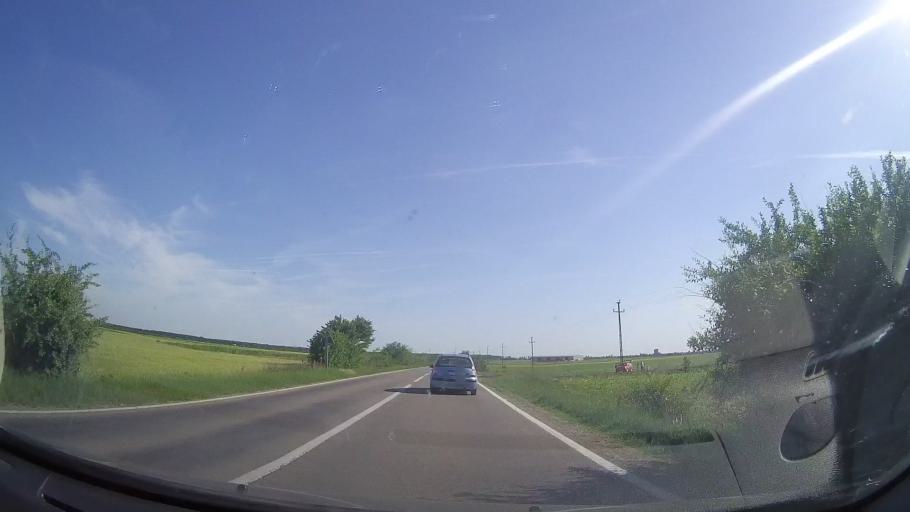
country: RO
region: Prahova
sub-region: Comuna Berceni
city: Berceni
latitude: 44.9316
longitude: 26.1039
